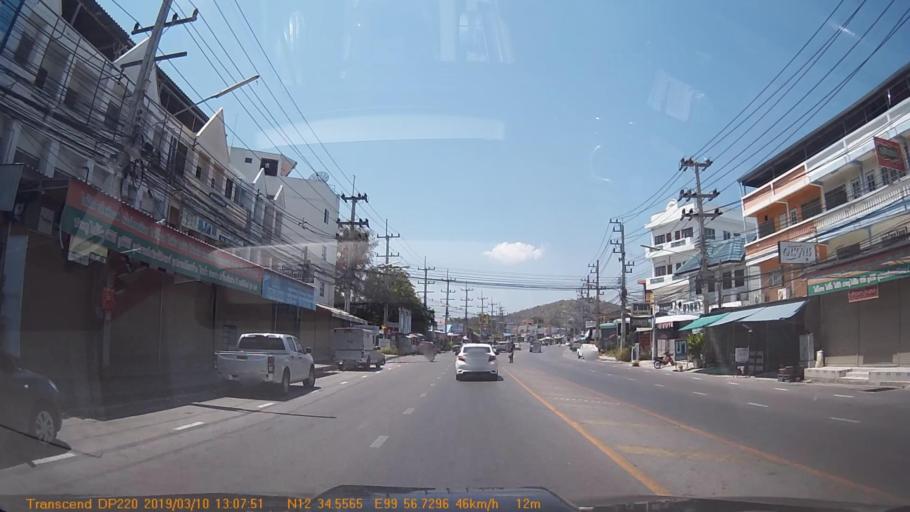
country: TH
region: Prachuap Khiri Khan
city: Hua Hin
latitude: 12.5760
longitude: 99.9454
